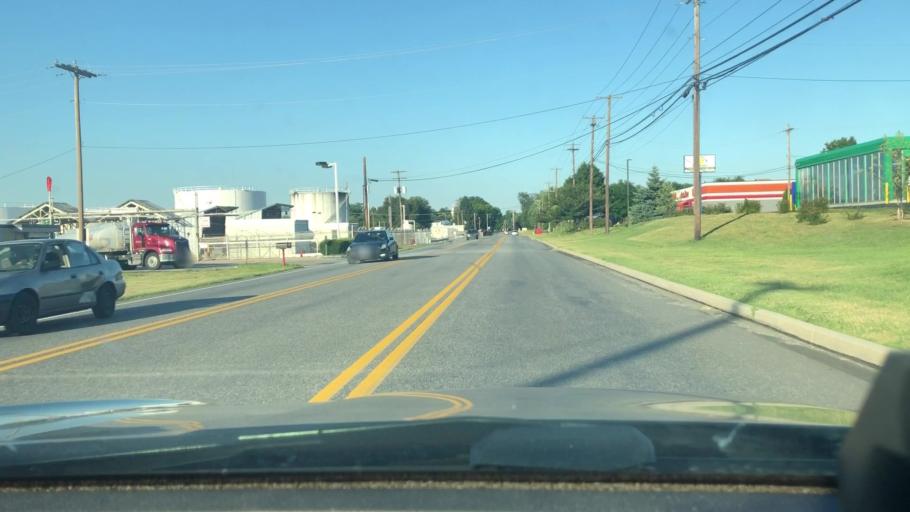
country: US
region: Pennsylvania
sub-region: Cumberland County
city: Shiremanstown
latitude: 40.2198
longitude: -76.9710
